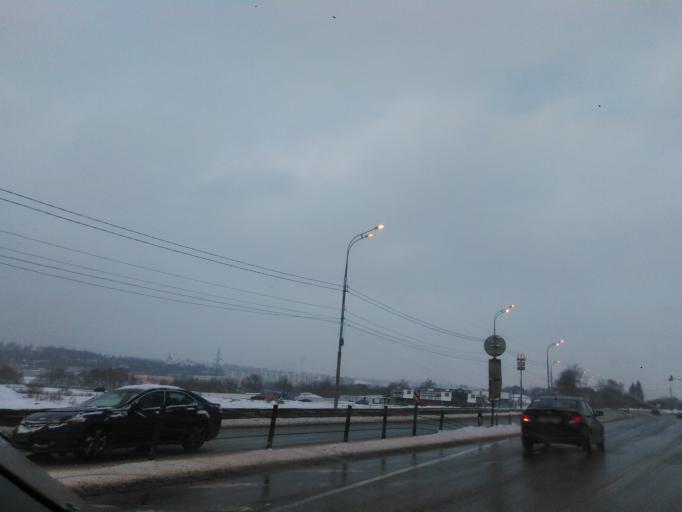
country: RU
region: Moskovskaya
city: Yakhroma
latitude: 56.2784
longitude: 37.5038
